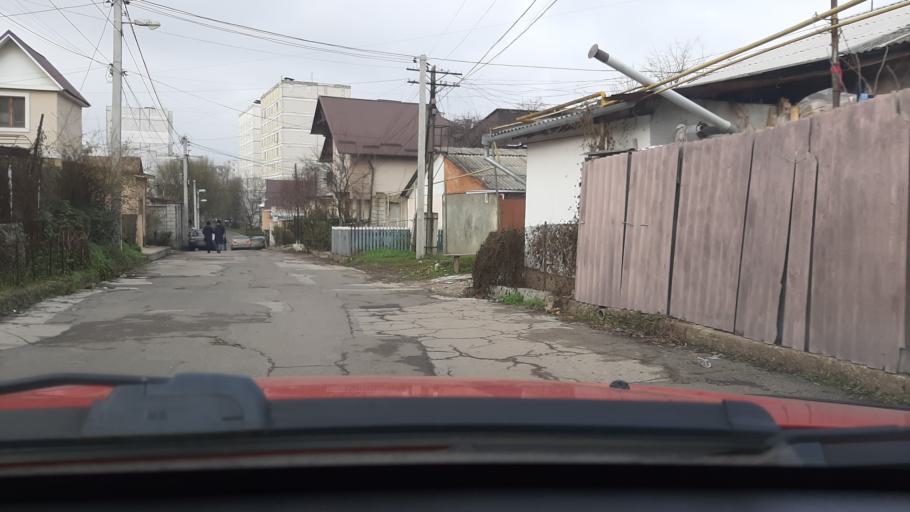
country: MD
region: Chisinau
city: Chisinau
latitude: 47.0331
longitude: 28.8330
